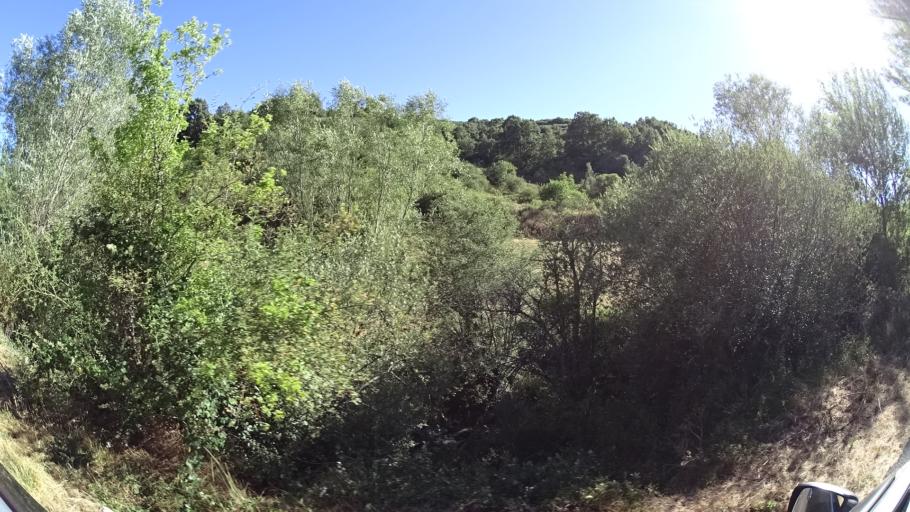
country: ES
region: Castille and Leon
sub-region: Provincia de Leon
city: La Pola de Gordon
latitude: 42.8971
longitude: -5.7000
